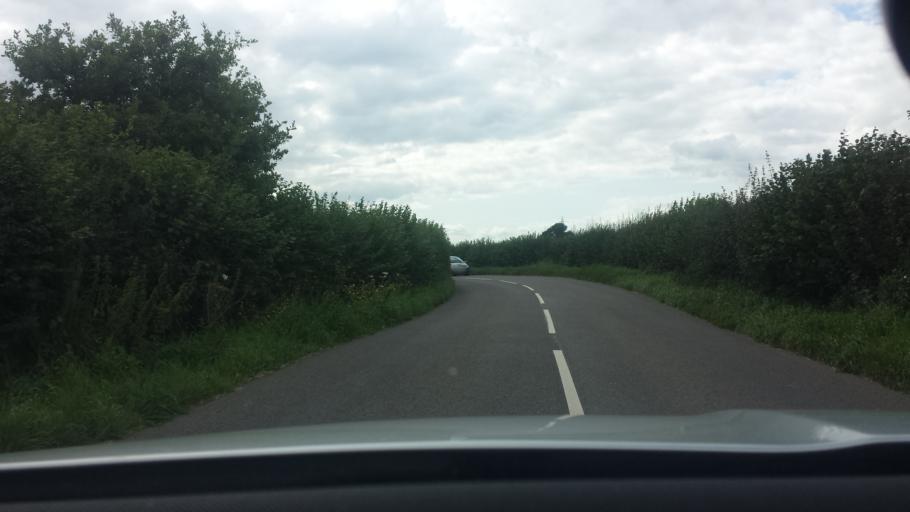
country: GB
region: England
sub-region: Kent
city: Marden
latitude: 51.1845
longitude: 0.4752
